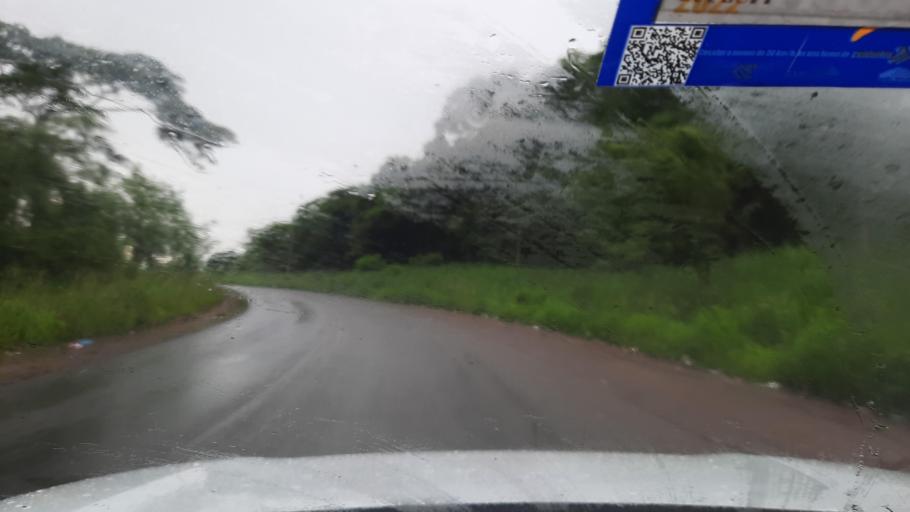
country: NI
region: Rivas
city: Cardenas
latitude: 11.1848
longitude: -85.6165
